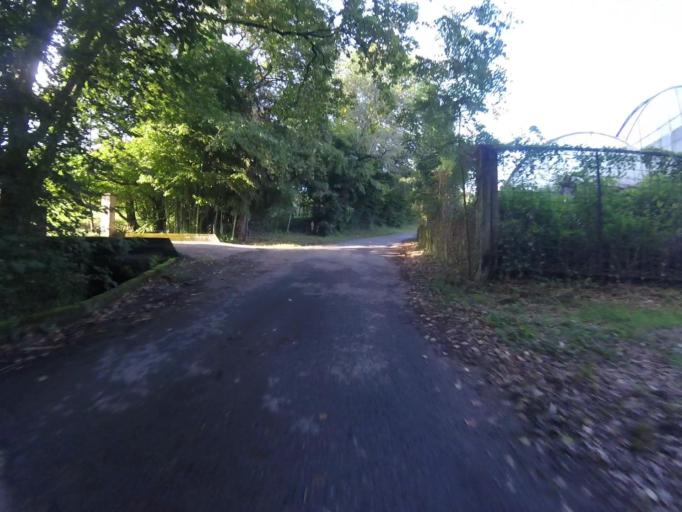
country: ES
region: Basque Country
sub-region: Provincia de Guipuzcoa
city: Fuenterrabia
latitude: 43.3610
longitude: -1.8085
